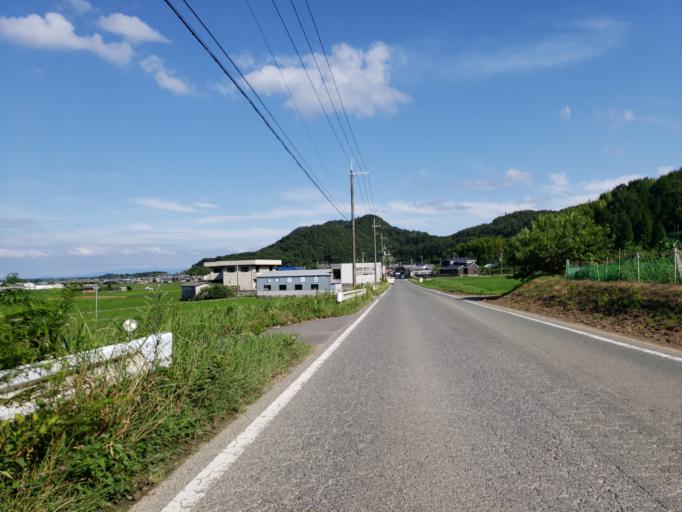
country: JP
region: Hyogo
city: Himeji
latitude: 34.8981
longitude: 134.7995
